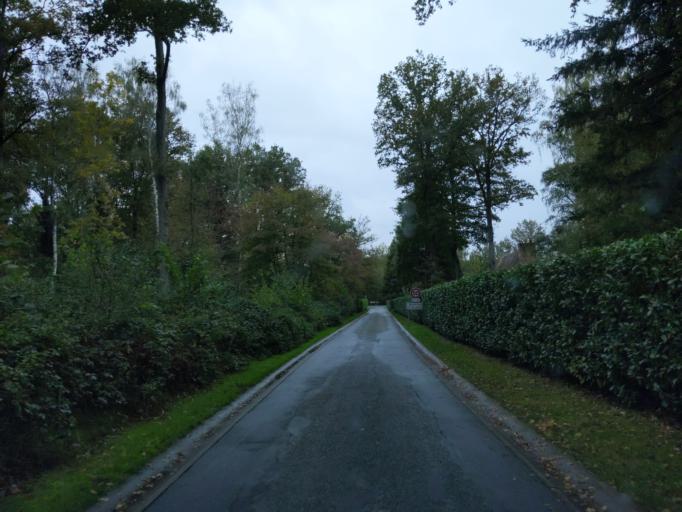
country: FR
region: Ile-de-France
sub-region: Departement des Yvelines
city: Bullion
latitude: 48.6104
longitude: 1.9787
